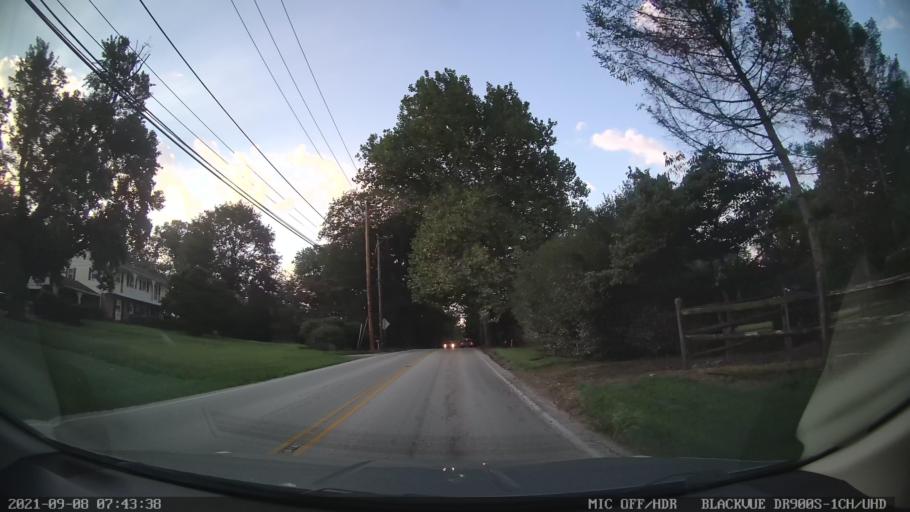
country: US
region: Pennsylvania
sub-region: Delaware County
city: Wayne
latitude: 40.0675
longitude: -75.3769
